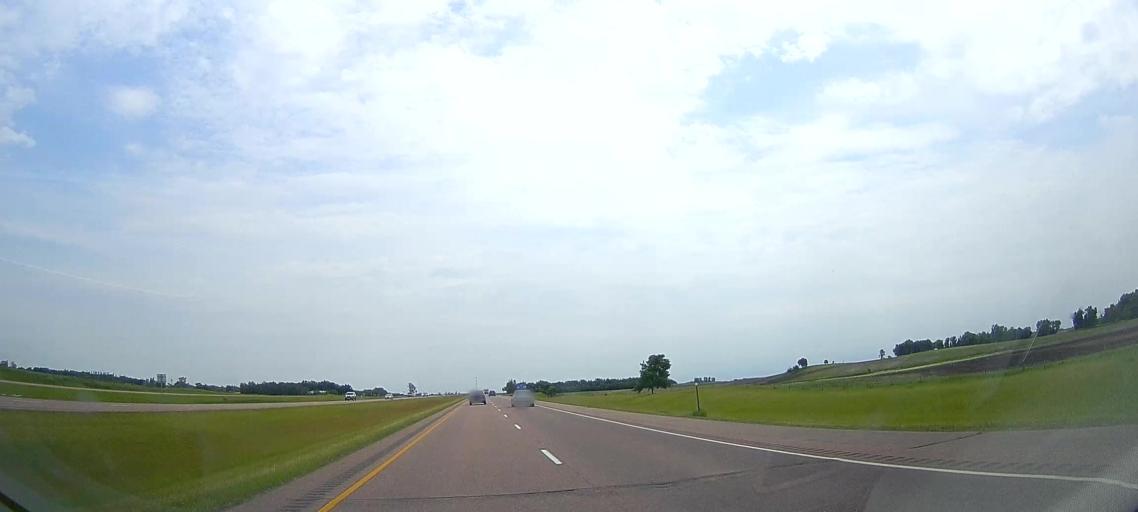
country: US
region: South Dakota
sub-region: Minnehaha County
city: Hartford
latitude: 43.6519
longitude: -97.1004
